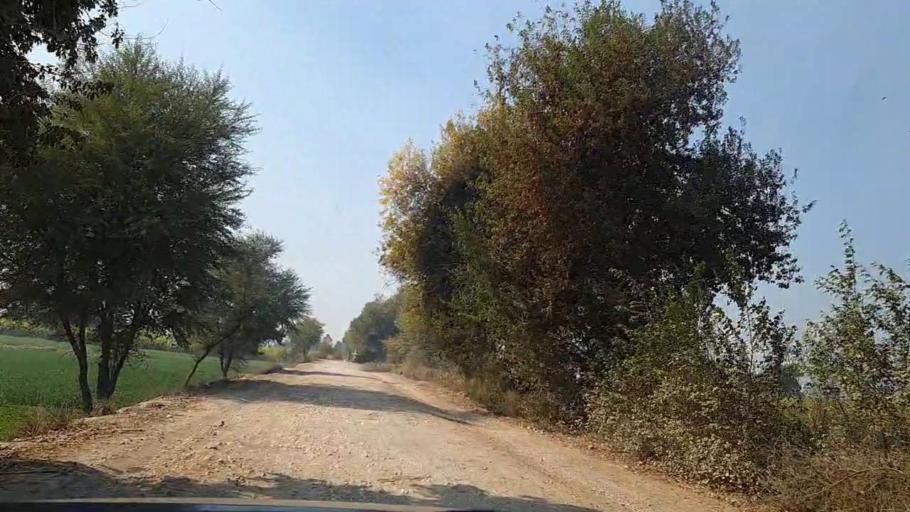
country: PK
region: Sindh
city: Daulatpur
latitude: 26.2904
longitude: 68.0695
